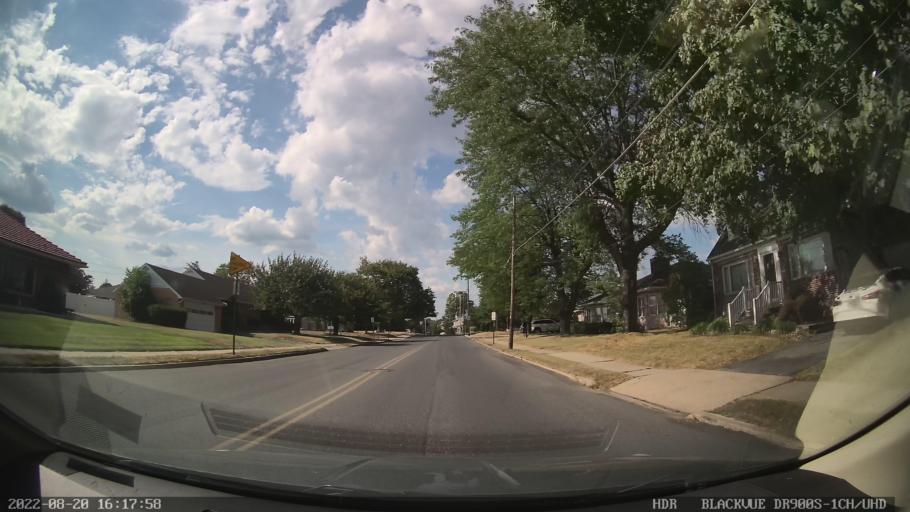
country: US
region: Pennsylvania
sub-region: Northampton County
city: Northampton
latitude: 40.6899
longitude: -75.4930
